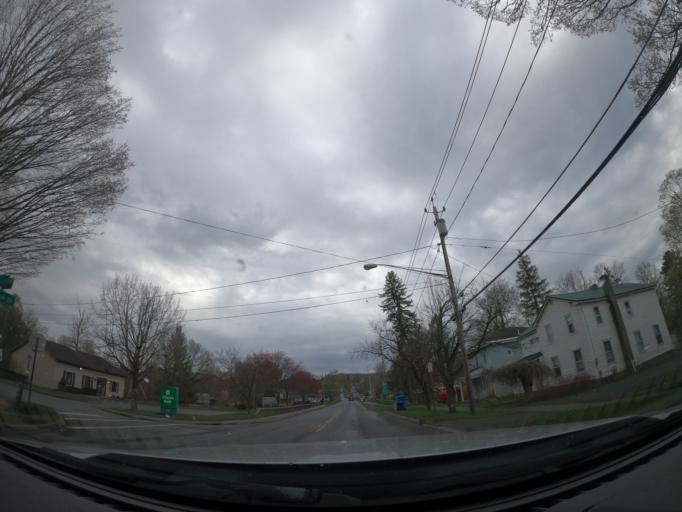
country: US
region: New York
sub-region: Madison County
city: Cazenovia
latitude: 42.7602
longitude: -75.8844
